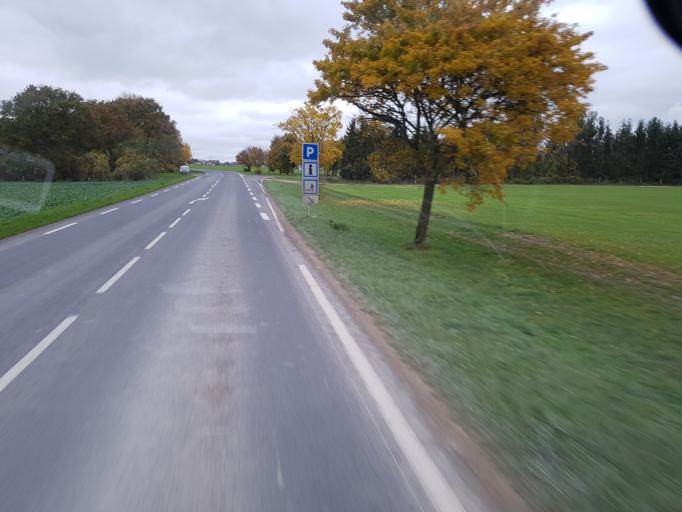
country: FR
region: Champagne-Ardenne
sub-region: Departement de la Marne
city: Saint-Just-Sauvage
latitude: 48.5872
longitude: 3.8296
